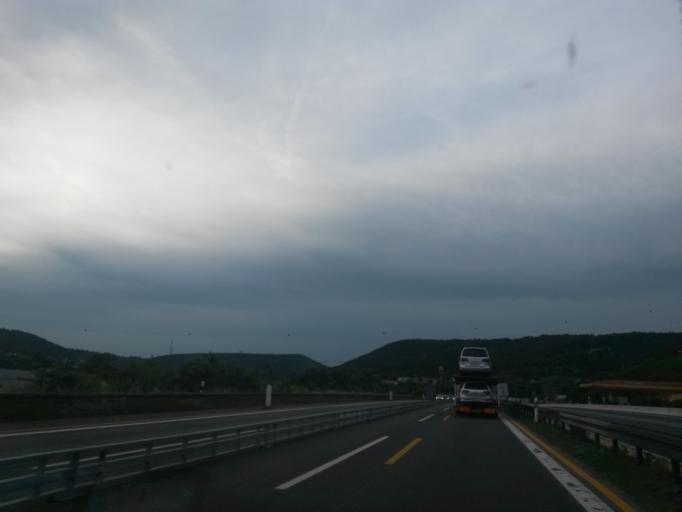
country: DE
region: Bavaria
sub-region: Regierungsbezirk Mittelfranken
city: Greding
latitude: 49.0478
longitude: 11.3357
